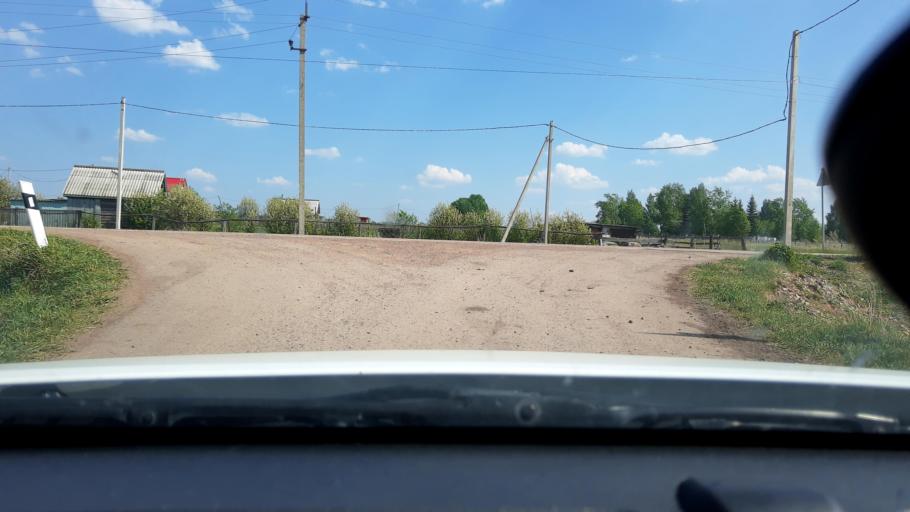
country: RU
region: Bashkortostan
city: Asanovo
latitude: 54.8431
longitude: 55.4585
